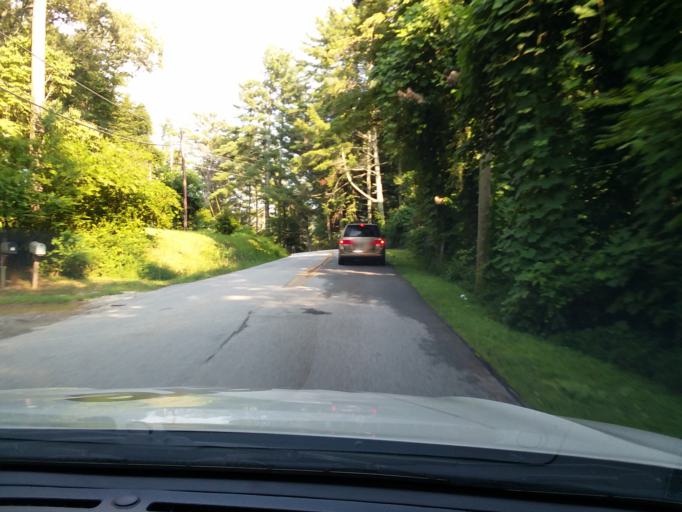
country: US
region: Georgia
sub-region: Rabun County
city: Clayton
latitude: 34.7744
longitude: -83.4242
